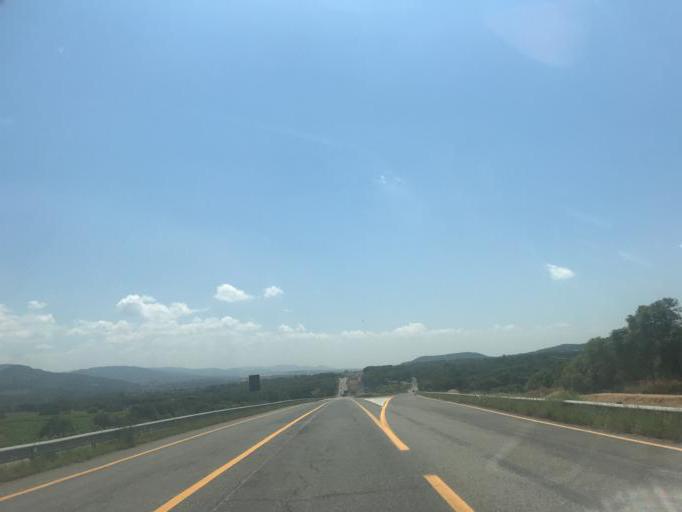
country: IT
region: Sardinia
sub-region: Provincia di Olbia-Tempio
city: Monti
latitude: 40.7992
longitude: 9.2751
